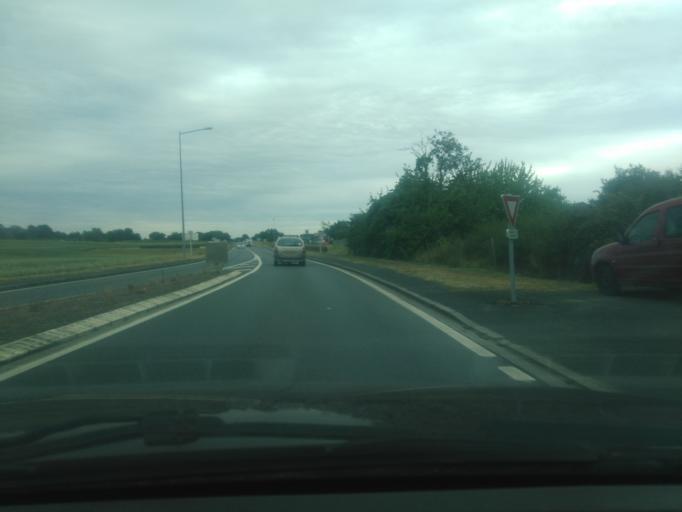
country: FR
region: Centre
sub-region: Departement de l'Indre
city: Saint-Marcel
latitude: 46.6240
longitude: 1.4892
